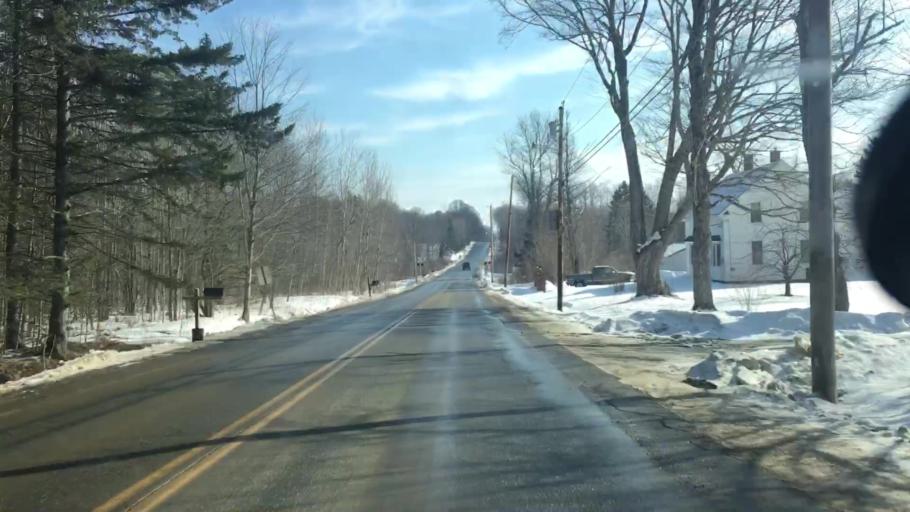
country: US
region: Maine
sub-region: Penobscot County
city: Hermon
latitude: 44.8516
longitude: -68.8437
